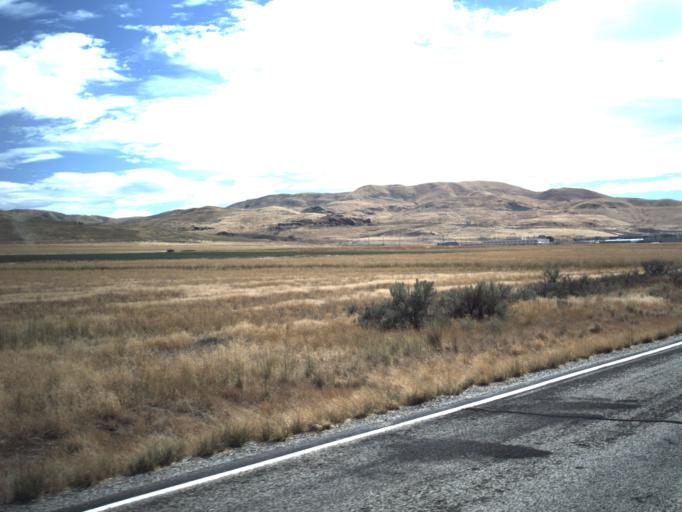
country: US
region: Utah
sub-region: Box Elder County
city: Tremonton
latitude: 41.7324
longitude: -112.4340
